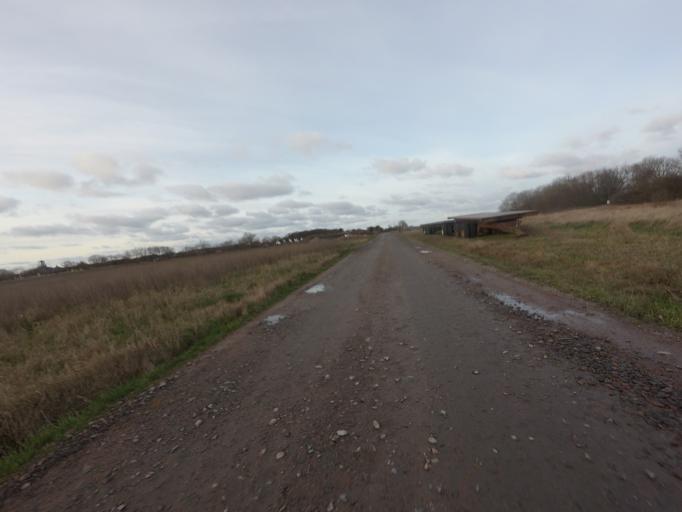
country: SE
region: Skane
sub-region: Hoganas Kommun
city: Hoganas
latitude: 56.1627
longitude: 12.5818
